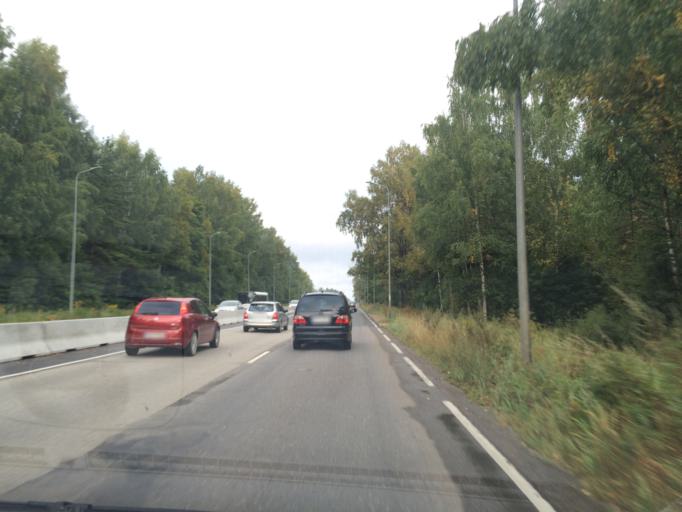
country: LV
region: Kekava
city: Kekava
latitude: 56.8742
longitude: 24.2650
